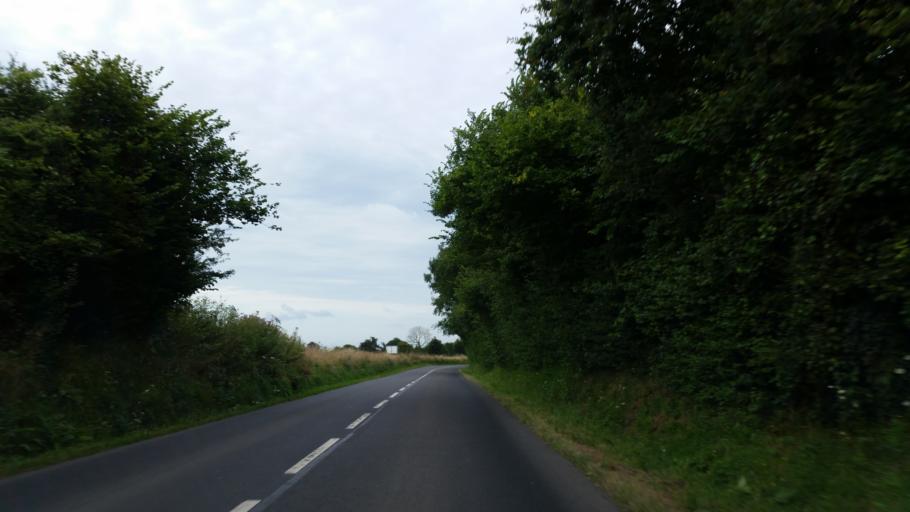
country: FR
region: Lower Normandy
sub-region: Departement du Calvados
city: Le Molay-Littry
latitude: 49.3532
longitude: -0.8841
